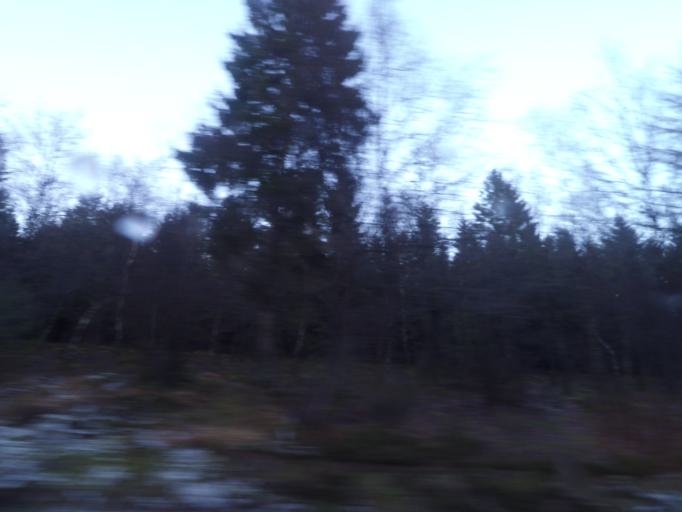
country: DK
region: Central Jutland
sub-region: Ikast-Brande Kommune
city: Brande
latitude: 56.0102
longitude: 9.0617
